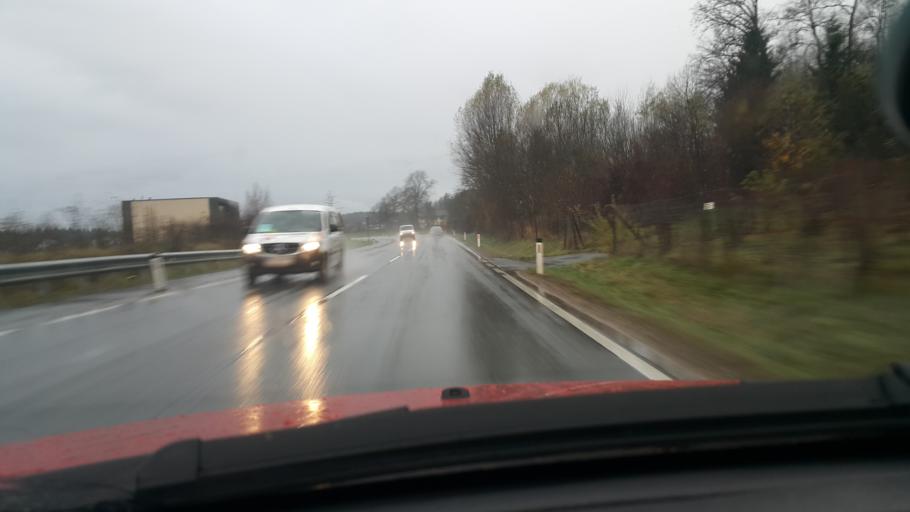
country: AT
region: Styria
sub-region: Politischer Bezirk Leibnitz
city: Hengsberg
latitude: 46.8649
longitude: 15.4598
